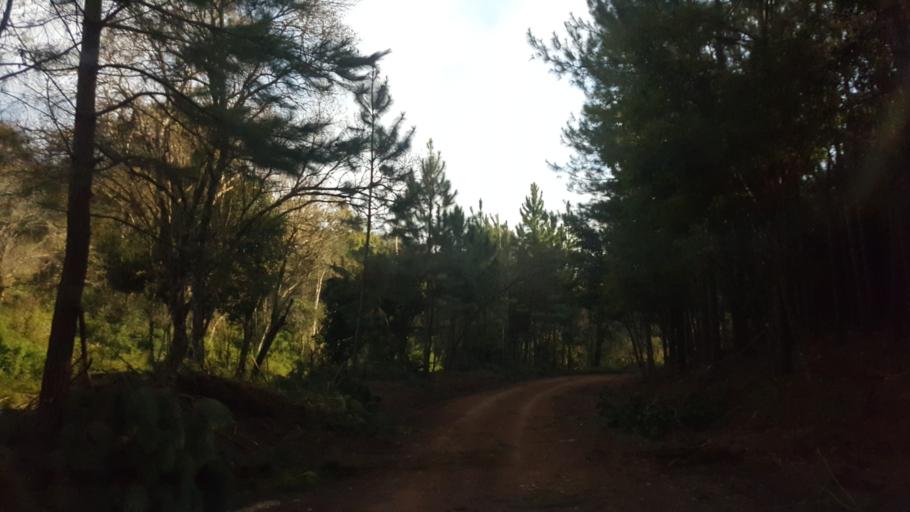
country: AR
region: Misiones
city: Capiovi
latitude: -26.9027
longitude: -55.0920
